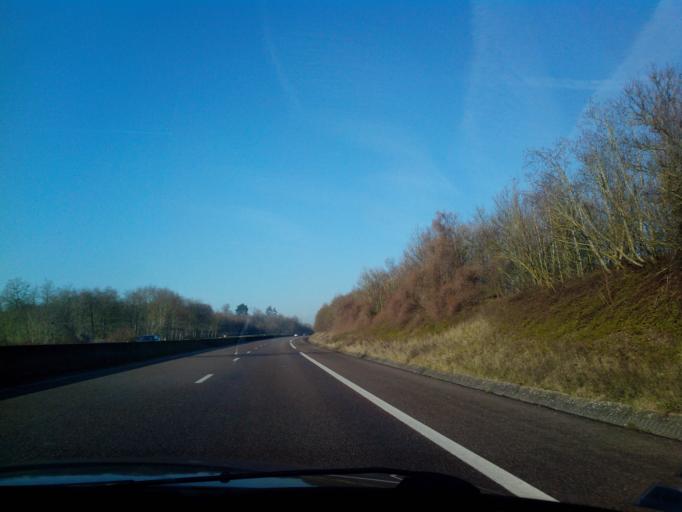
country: FR
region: Picardie
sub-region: Departement de l'Oise
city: Amblainville
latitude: 49.2213
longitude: 2.1167
